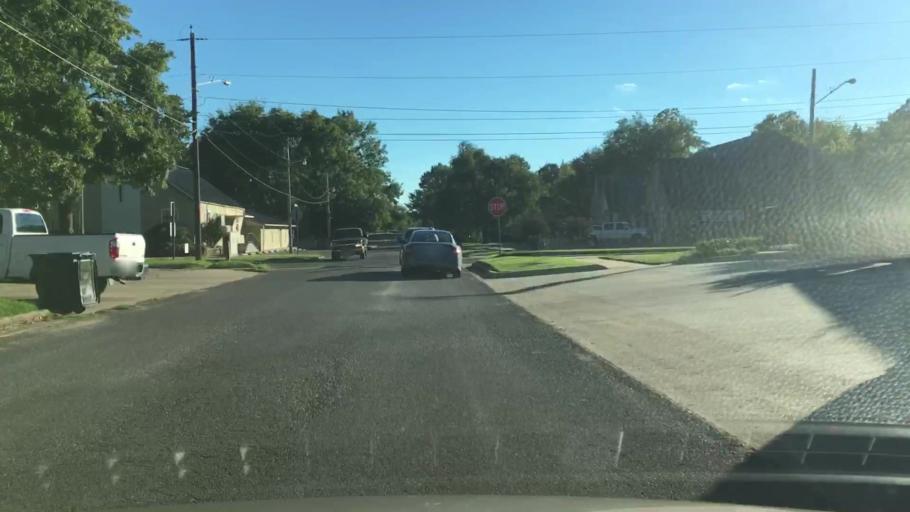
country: US
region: Oklahoma
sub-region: Cherokee County
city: Tahlequah
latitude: 35.9124
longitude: -94.9745
